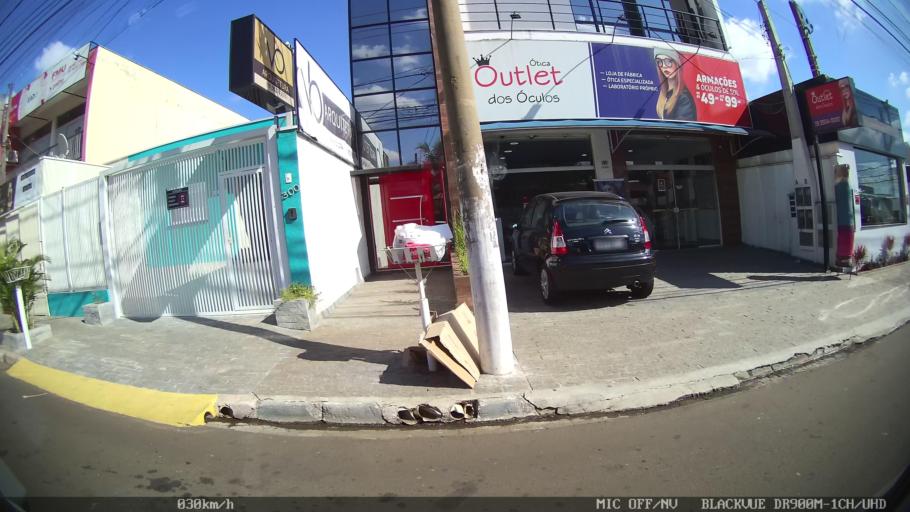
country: BR
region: Sao Paulo
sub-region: Hortolandia
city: Hortolandia
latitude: -22.8666
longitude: -47.2168
